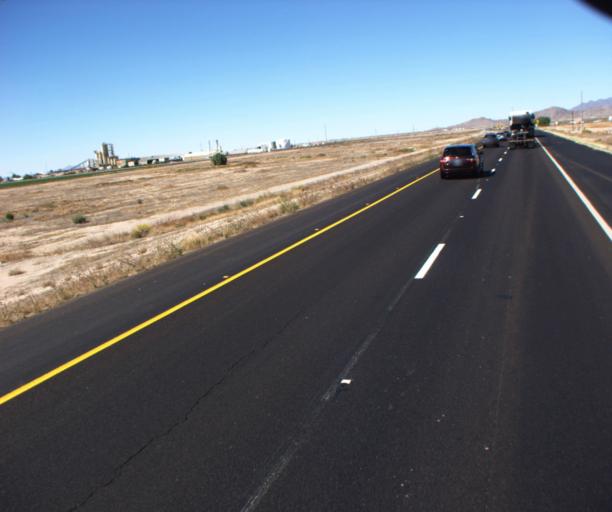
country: US
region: Arizona
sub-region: Maricopa County
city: Buckeye
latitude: 33.3719
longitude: -112.6248
